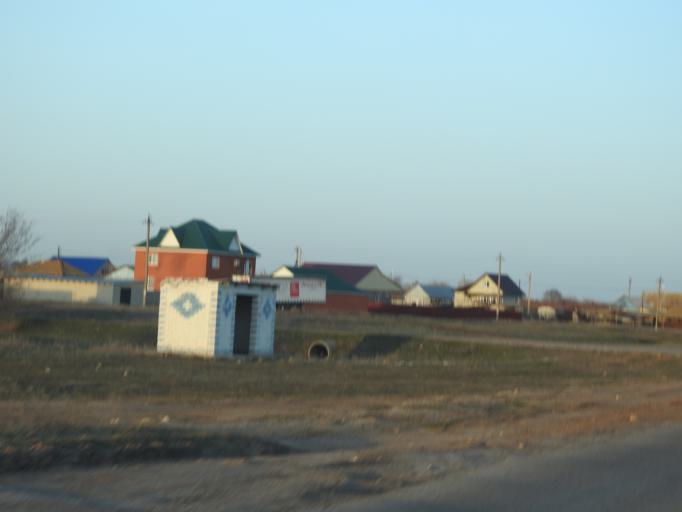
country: RU
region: Volgograd
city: Staraya Poltavka
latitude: 50.5016
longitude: 46.5173
